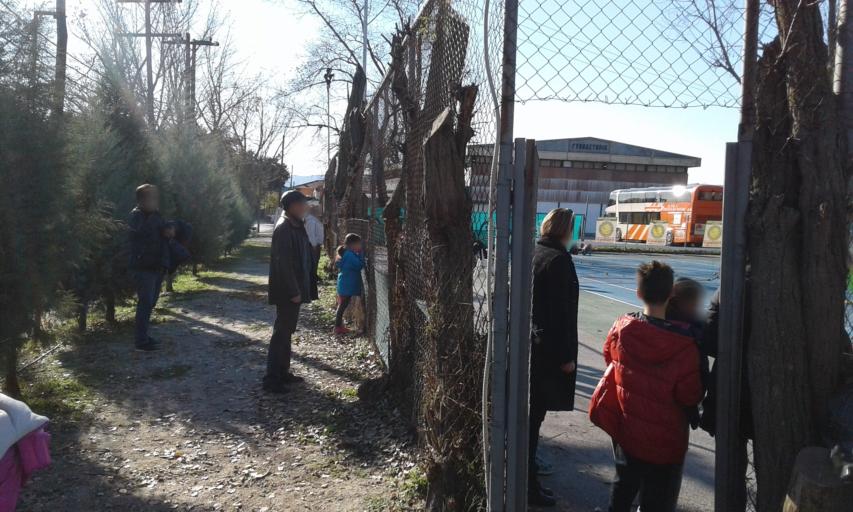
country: GR
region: Central Macedonia
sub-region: Nomos Thessalonikis
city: Lagkadas
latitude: 40.7485
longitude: 23.0599
